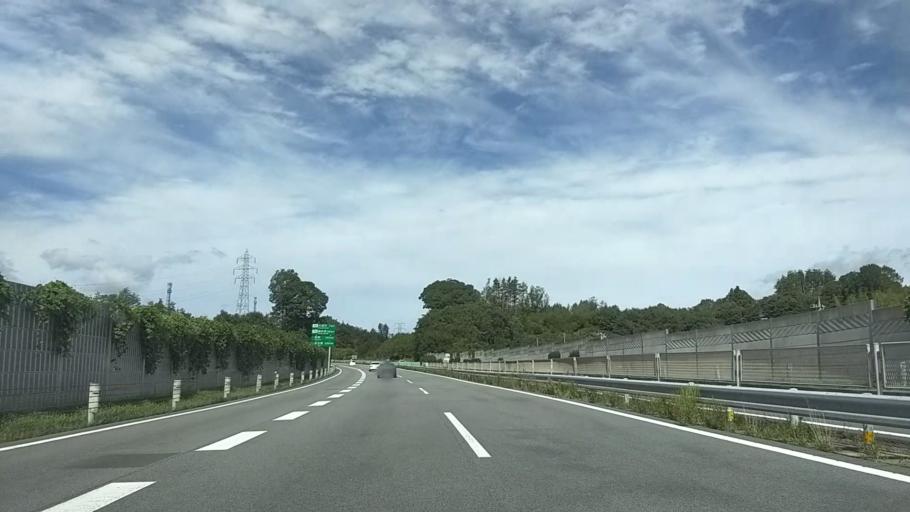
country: JP
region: Yamanashi
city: Nirasaki
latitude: 35.8431
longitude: 138.3794
